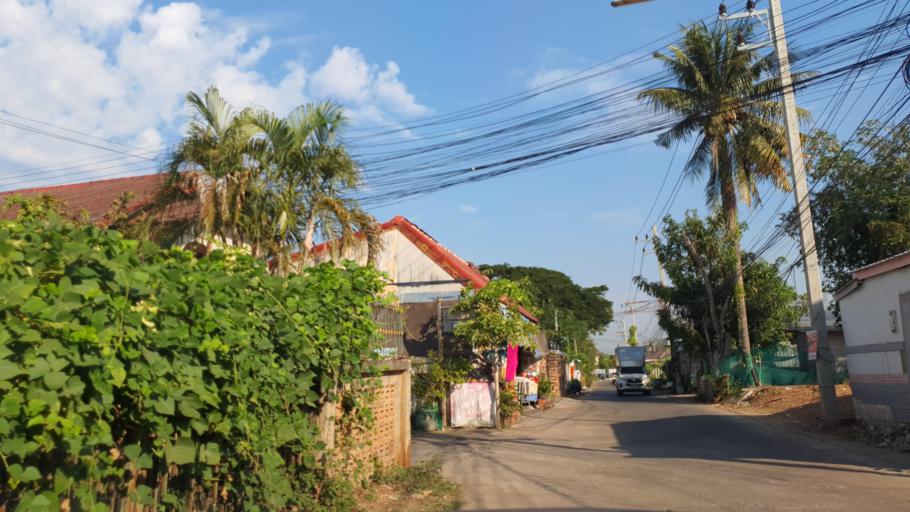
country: TH
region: Khon Kaen
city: Khon Kaen
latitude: 16.4129
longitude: 102.8068
